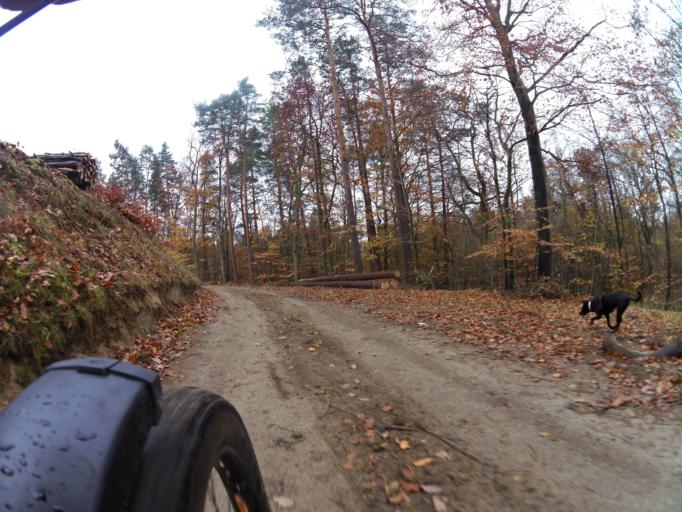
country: PL
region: Pomeranian Voivodeship
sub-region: Powiat pucki
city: Krokowa
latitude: 54.7488
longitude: 18.0902
